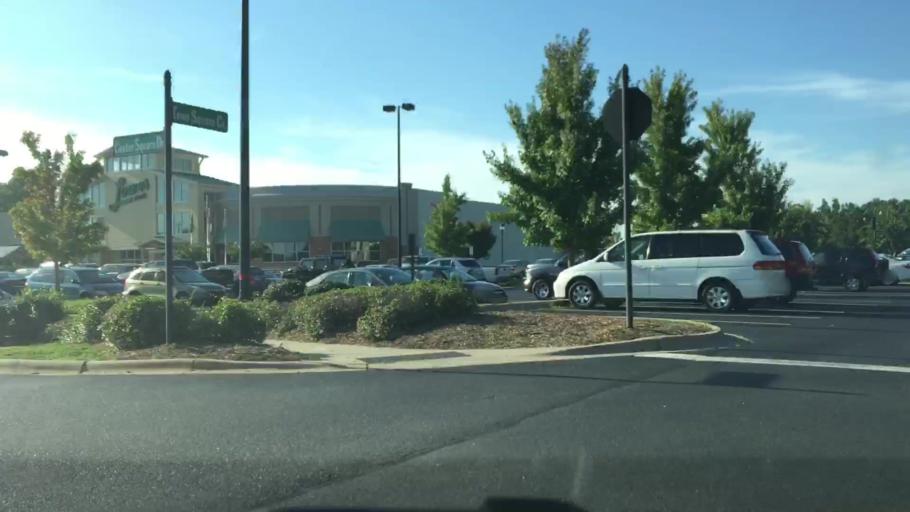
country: US
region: North Carolina
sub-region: Iredell County
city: Mooresville
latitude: 35.5869
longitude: -80.8713
